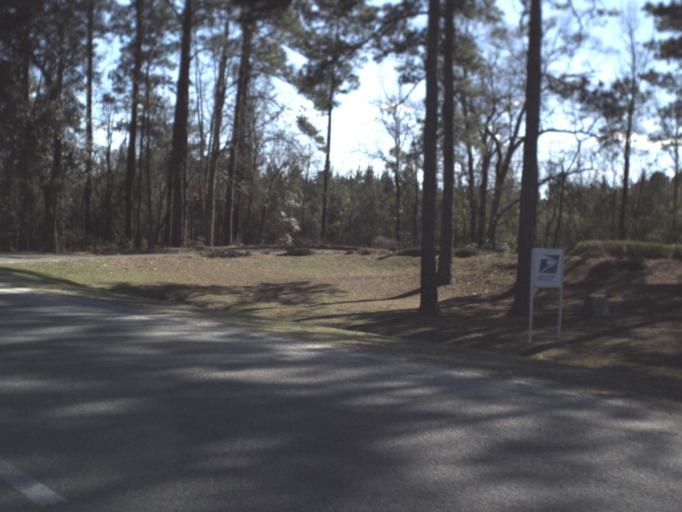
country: US
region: Florida
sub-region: Gadsden County
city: Midway
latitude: 30.5045
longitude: -84.4533
